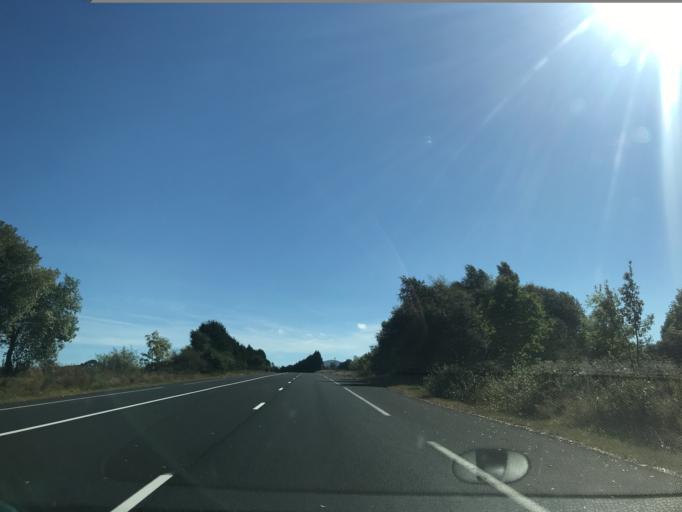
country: FR
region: Auvergne
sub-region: Departement du Puy-de-Dome
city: La Bourboule
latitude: 45.6639
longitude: 2.7472
